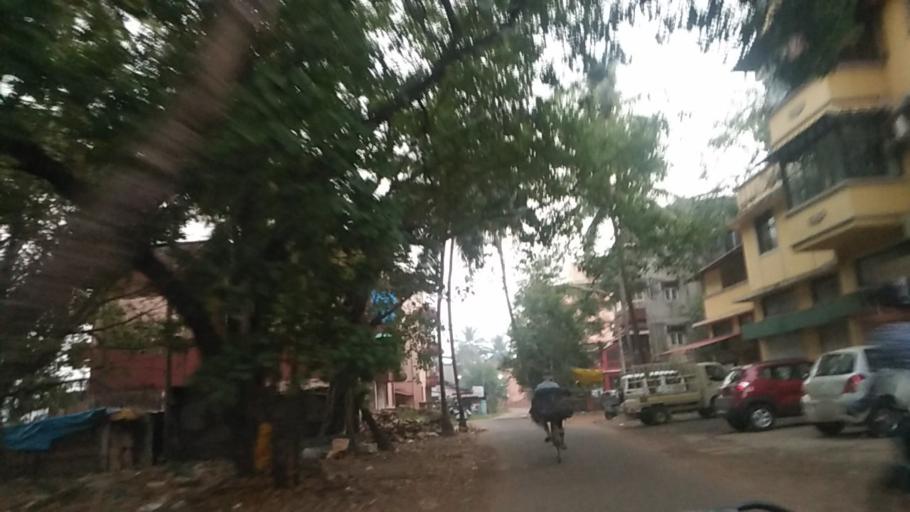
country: IN
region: Goa
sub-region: South Goa
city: Madgaon
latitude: 15.2871
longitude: 73.9547
